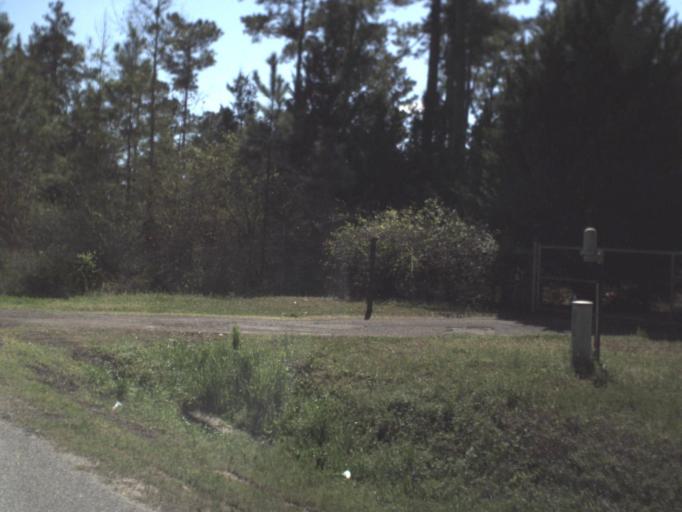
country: US
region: Florida
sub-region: Gadsden County
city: Quincy
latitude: 30.6257
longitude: -84.5975
